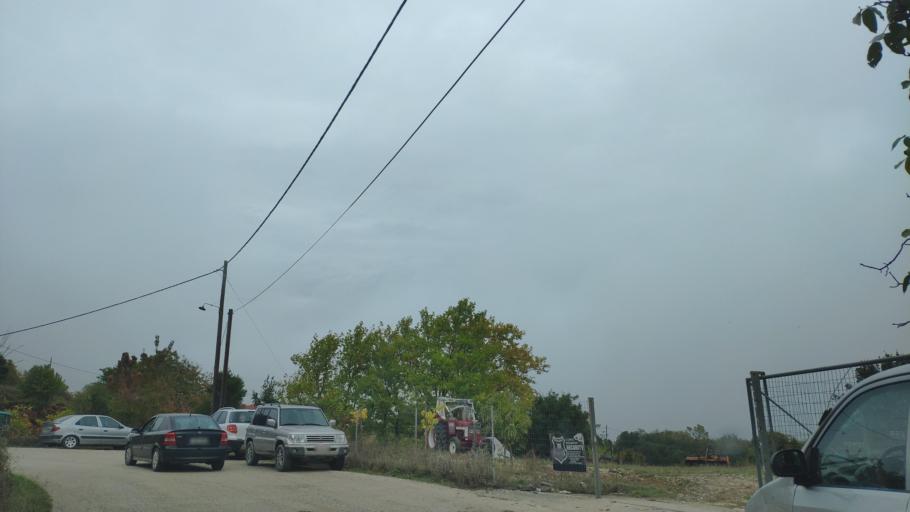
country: GR
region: Epirus
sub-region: Nomos Thesprotias
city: Paramythia
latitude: 39.4705
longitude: 20.6701
